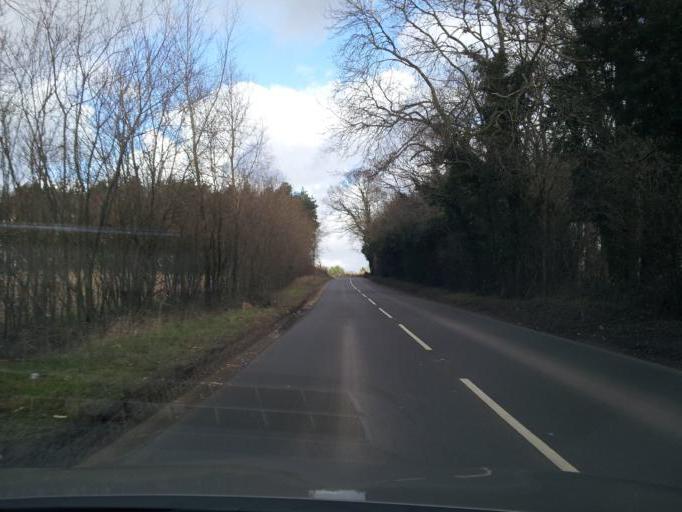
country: GB
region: England
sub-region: Norfolk
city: Mattishall
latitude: 52.6750
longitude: 1.1020
